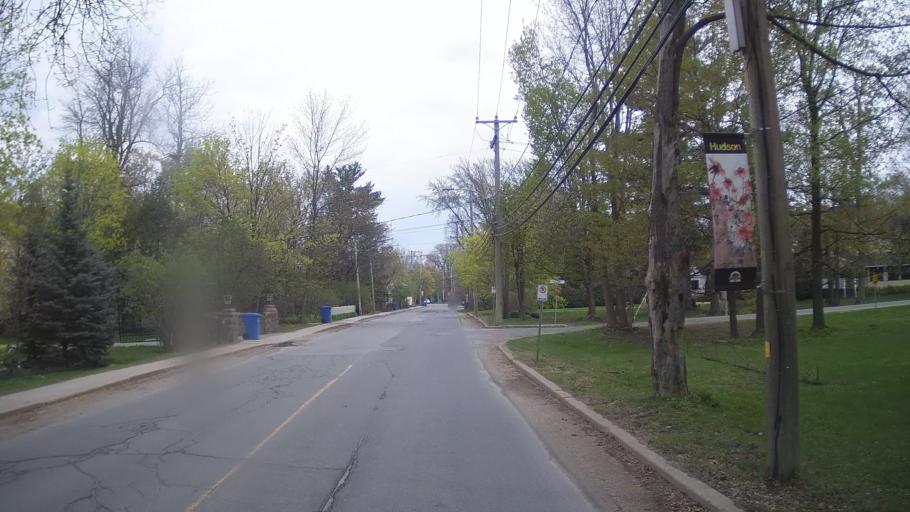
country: CA
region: Quebec
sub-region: Monteregie
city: Hudson
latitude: 45.4627
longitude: -74.1478
